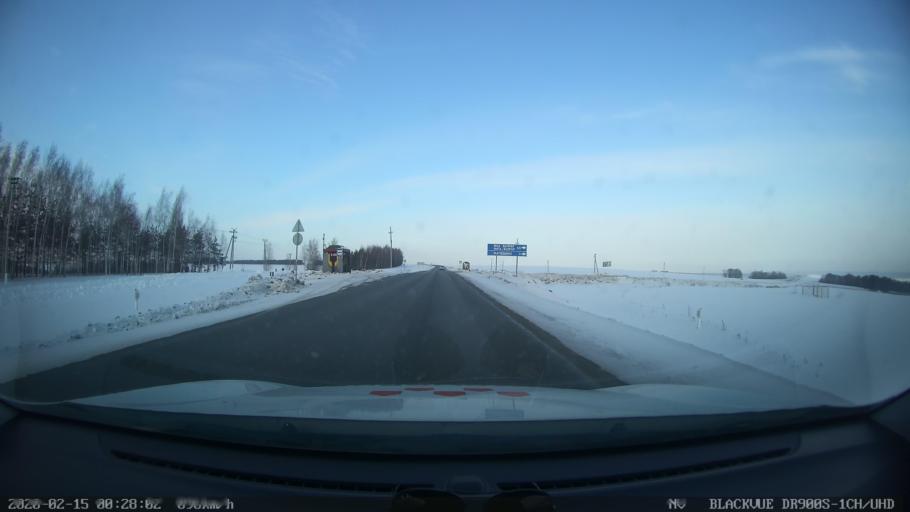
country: RU
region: Tatarstan
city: Verkhniy Uslon
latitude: 55.6367
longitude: 48.8731
